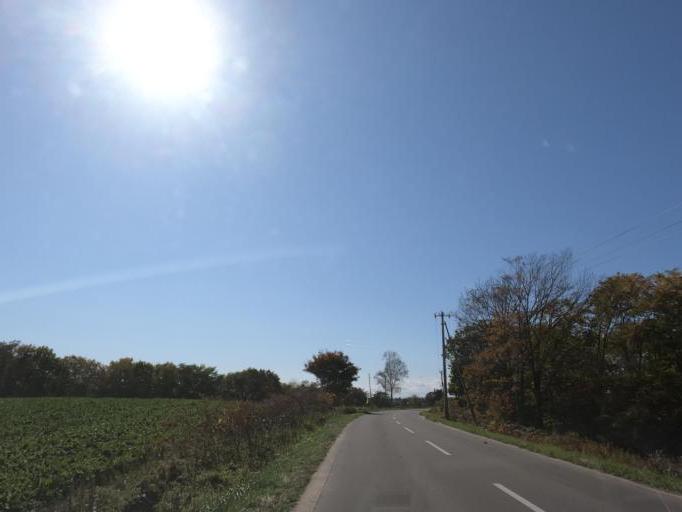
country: JP
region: Hokkaido
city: Obihiro
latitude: 42.8253
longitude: 143.2588
